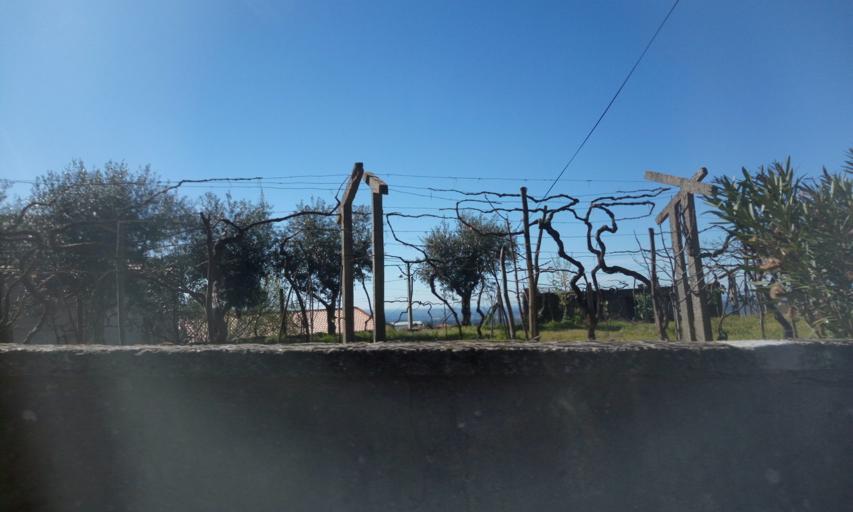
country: PT
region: Guarda
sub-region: Manteigas
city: Manteigas
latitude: 40.4918
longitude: -7.5882
